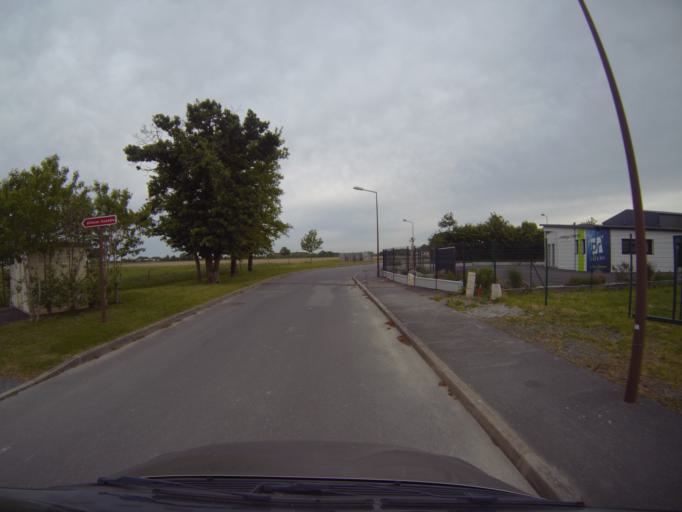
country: FR
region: Pays de la Loire
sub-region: Departement de la Loire-Atlantique
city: La Planche
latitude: 47.0201
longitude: -1.4264
